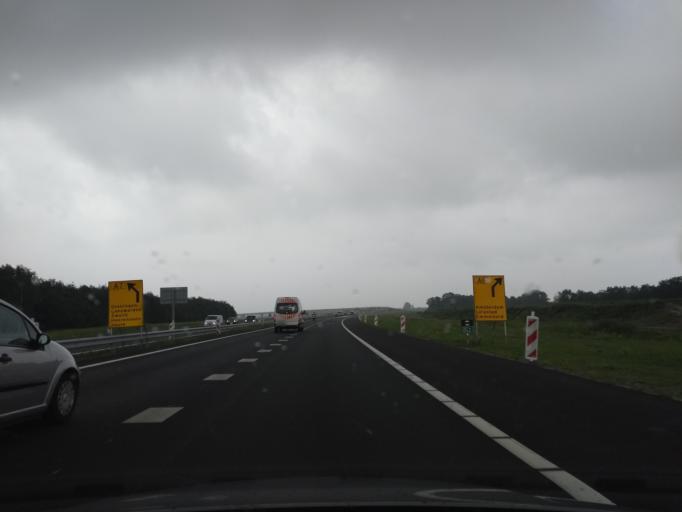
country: NL
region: Friesland
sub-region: Gemeente Skarsterlan
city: Joure
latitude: 52.9522
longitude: 5.7919
